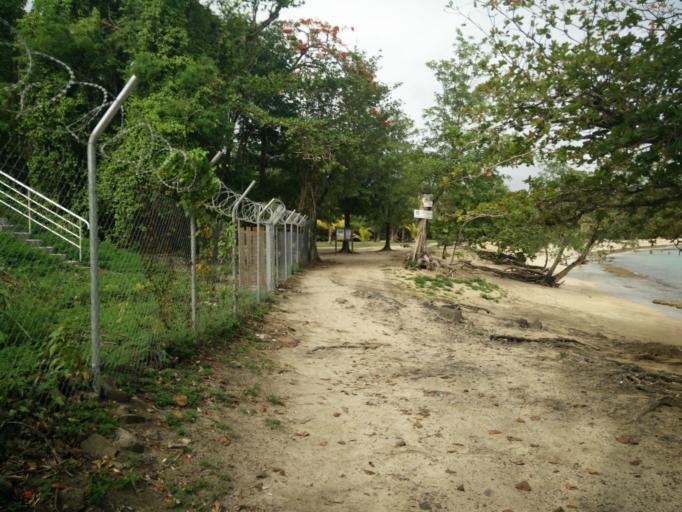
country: MQ
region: Martinique
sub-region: Martinique
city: Sainte-Luce
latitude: 14.4683
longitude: -60.9590
